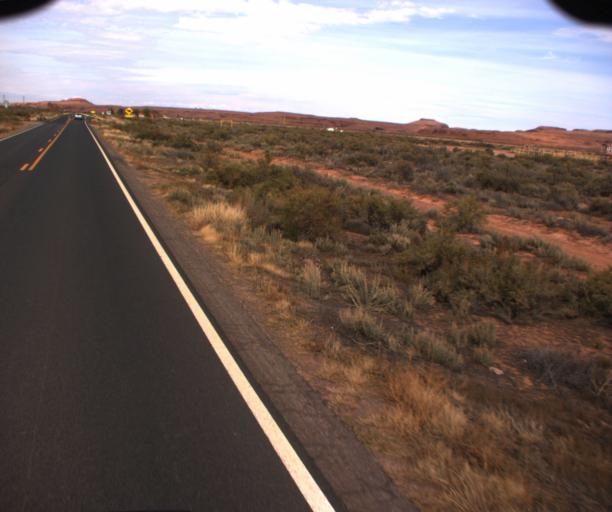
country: US
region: Arizona
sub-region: Apache County
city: Many Farms
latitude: 36.7238
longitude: -109.6291
